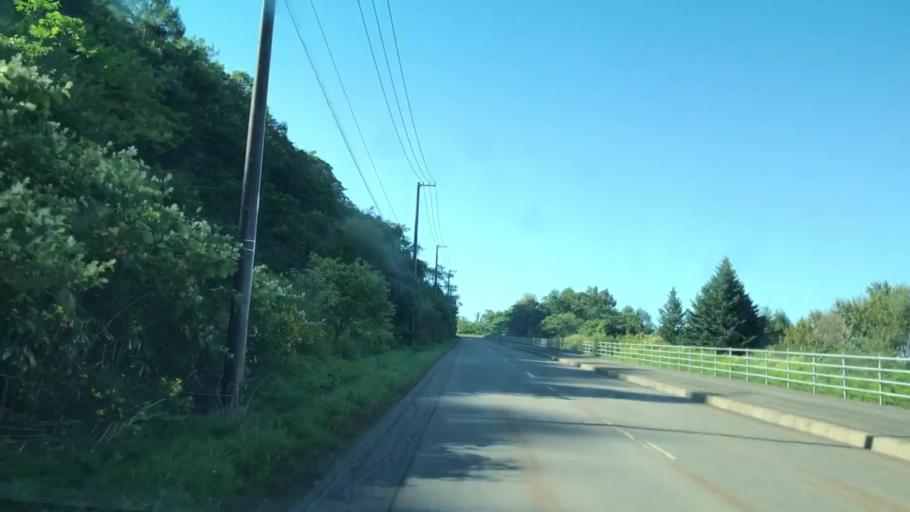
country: JP
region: Hokkaido
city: Date
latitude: 42.5636
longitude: 140.8076
